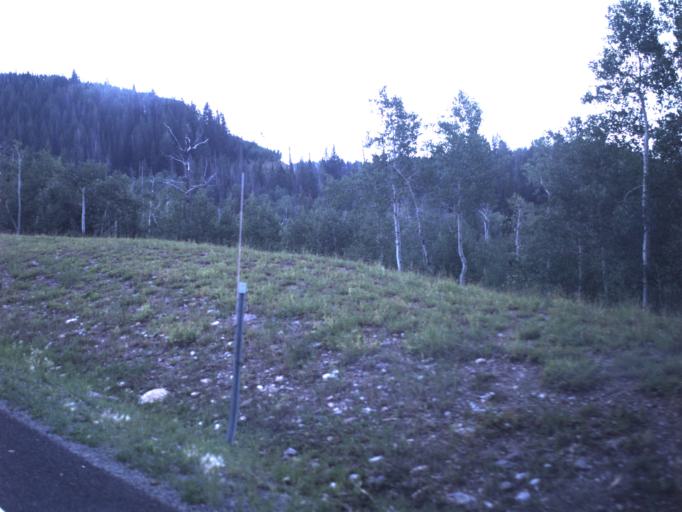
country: US
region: Utah
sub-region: Summit County
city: Francis
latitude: 40.5132
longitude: -111.0458
